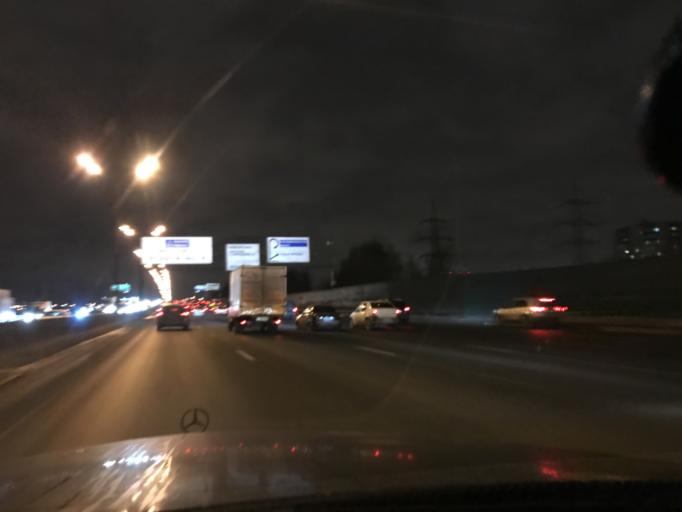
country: RU
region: Moscow
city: Ivanovskoye
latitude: 55.7541
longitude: 37.8422
